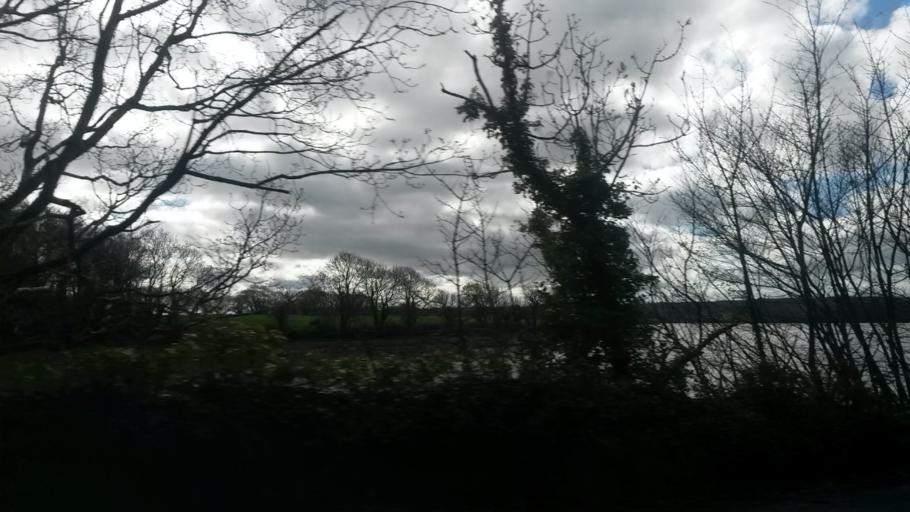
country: IE
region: Munster
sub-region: County Cork
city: Carrigtwohill
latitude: 51.8963
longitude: -8.2815
